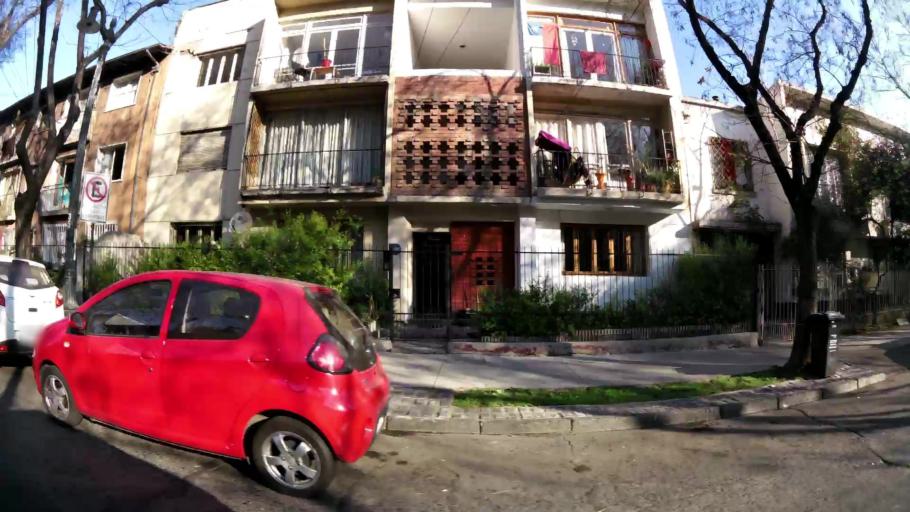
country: CL
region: Santiago Metropolitan
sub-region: Provincia de Santiago
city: Santiago
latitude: -33.4314
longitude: -70.6324
